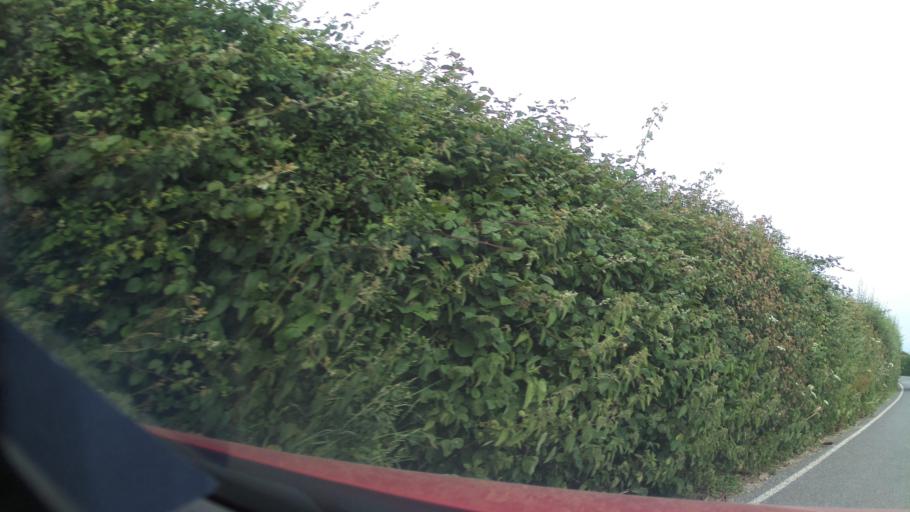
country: GB
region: England
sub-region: Devon
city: Colyton
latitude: 50.7086
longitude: -3.1046
